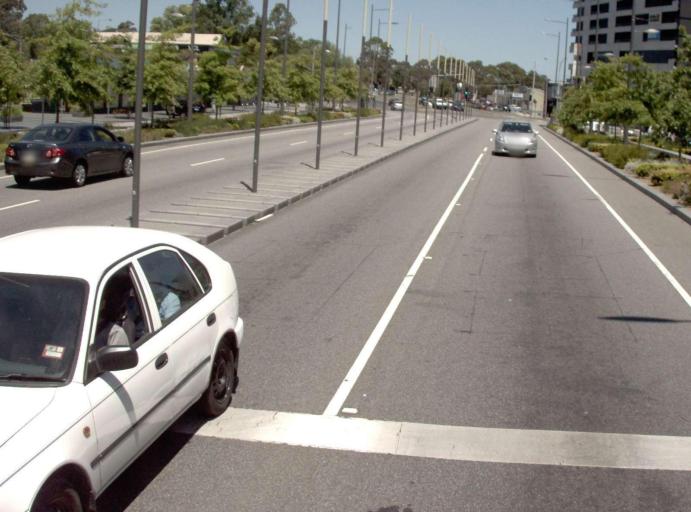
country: AU
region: Victoria
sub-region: Greater Dandenong
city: Dandenong
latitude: -37.9889
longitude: 145.2144
